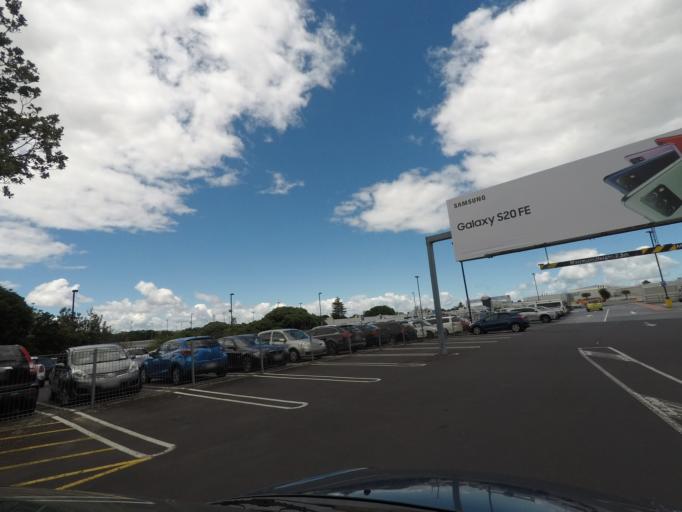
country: NZ
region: Auckland
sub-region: Auckland
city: Auckland
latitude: -36.8818
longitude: 174.7341
